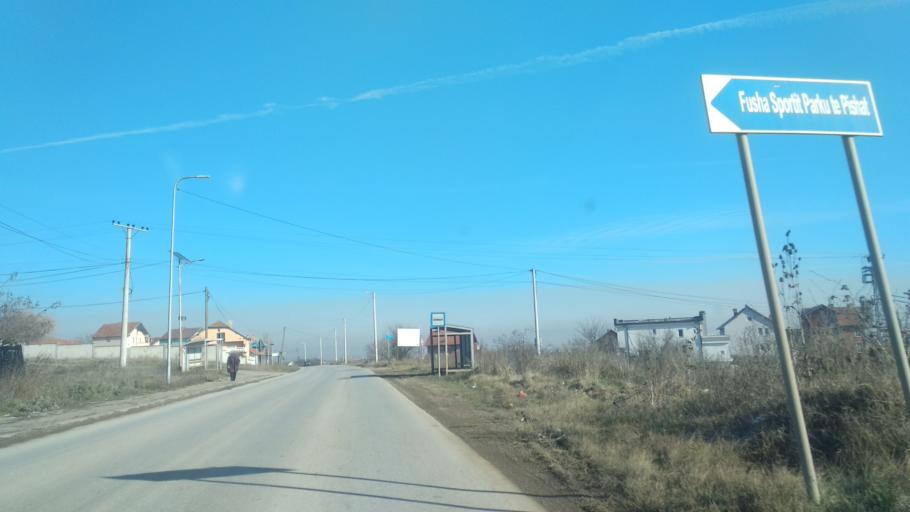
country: XK
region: Pristina
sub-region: Komuna e Gracanices
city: Glanica
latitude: 42.6034
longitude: 21.0277
